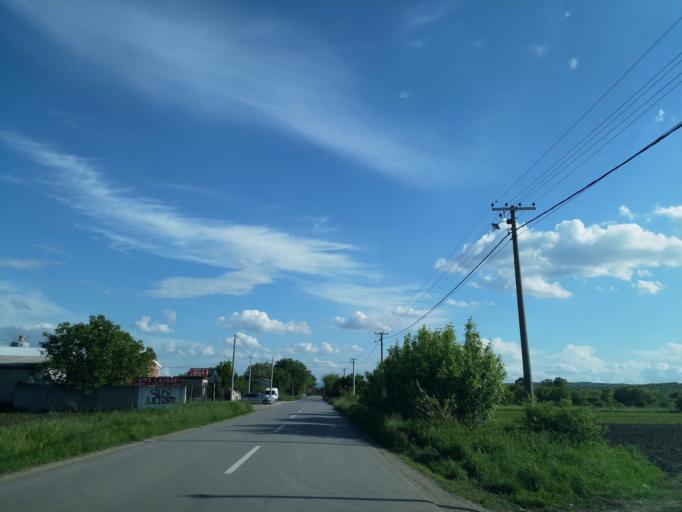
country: RS
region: Central Serbia
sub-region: Sumadijski Okrug
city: Lapovo
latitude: 44.2311
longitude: 21.0946
